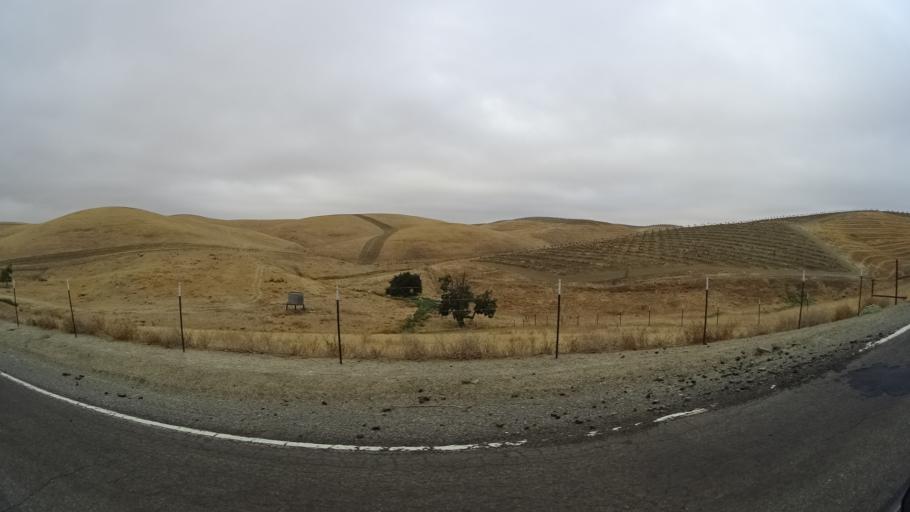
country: US
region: California
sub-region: Yolo County
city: Dunnigan
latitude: 38.8810
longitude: -122.0065
